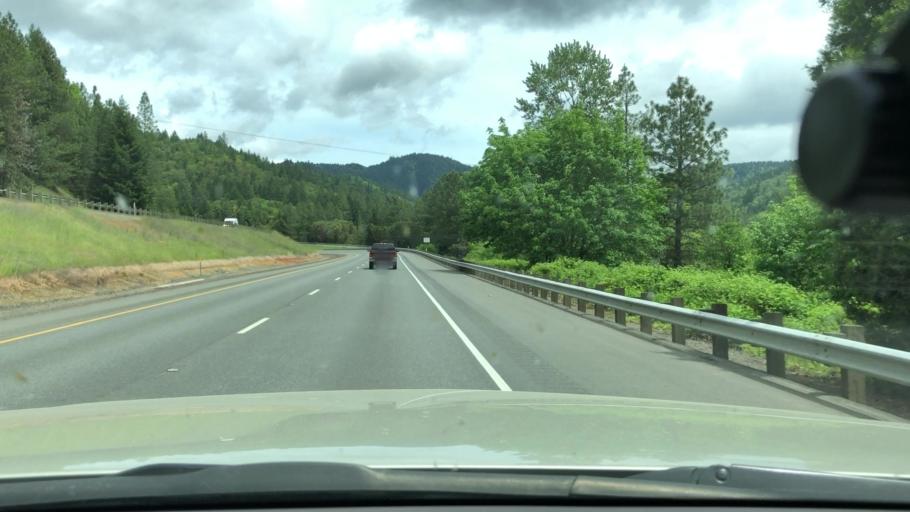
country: US
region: Oregon
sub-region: Josephine County
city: Merlin
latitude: 42.7059
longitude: -123.3699
